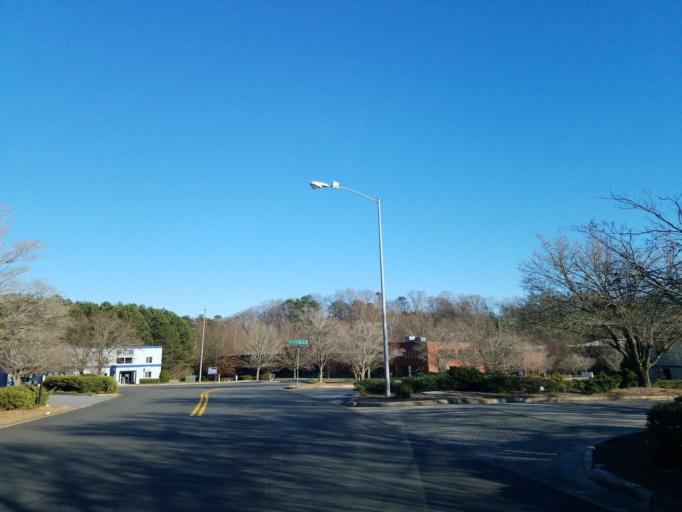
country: US
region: Georgia
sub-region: Cobb County
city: Marietta
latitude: 33.9705
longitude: -84.5247
